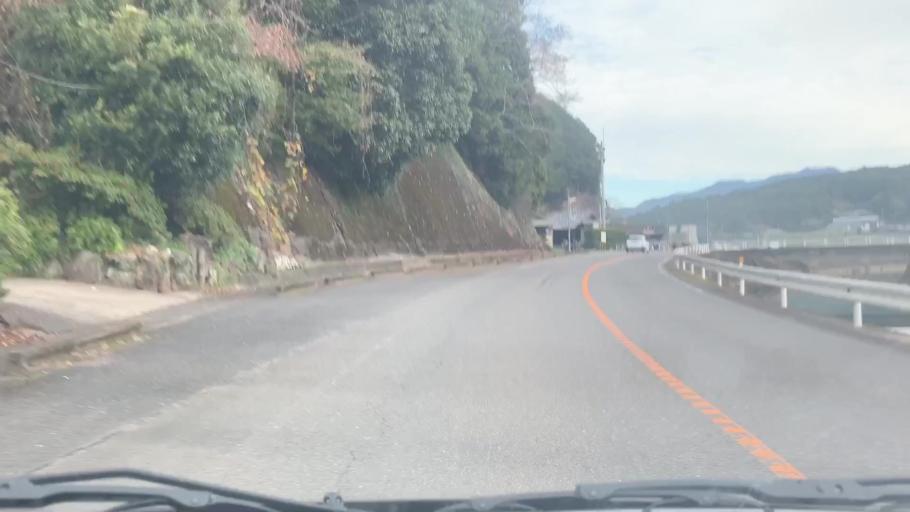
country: JP
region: Saga Prefecture
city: Takeocho-takeo
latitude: 33.2305
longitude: 129.9645
